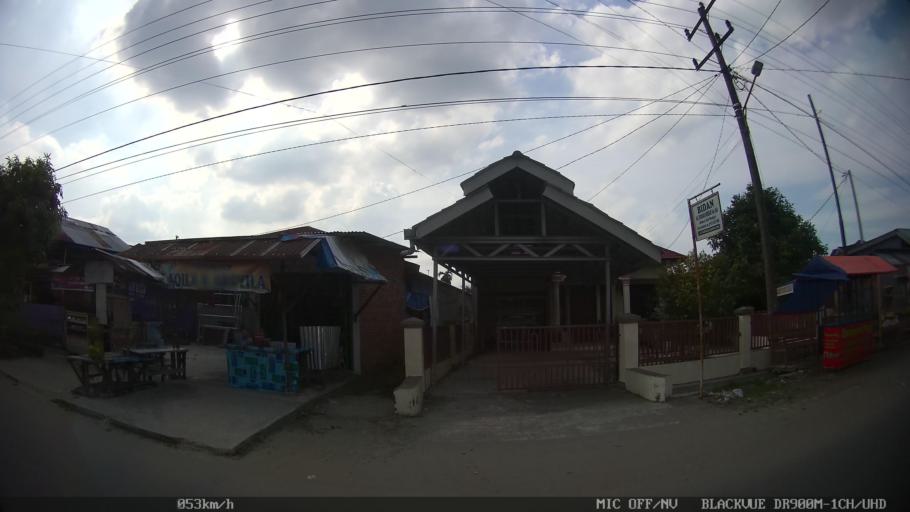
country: ID
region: North Sumatra
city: Binjai
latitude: 3.6389
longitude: 98.4932
